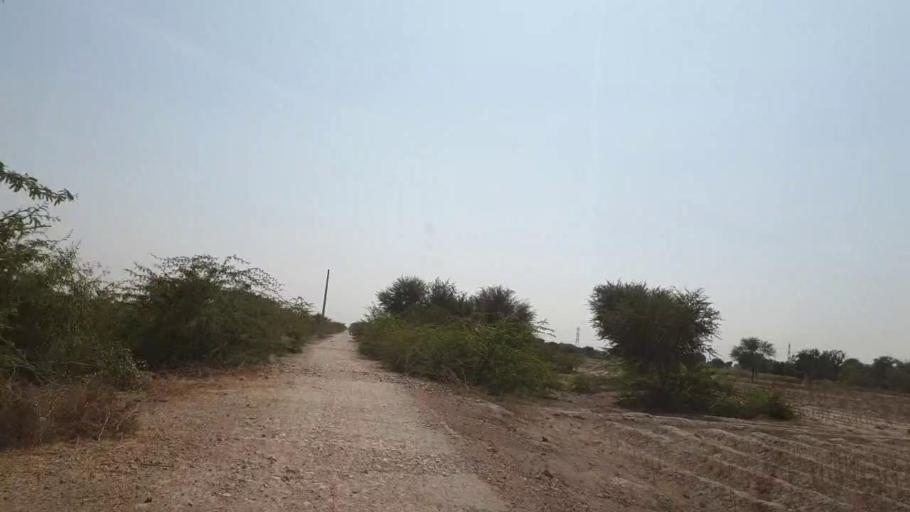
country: PK
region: Sindh
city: Nabisar
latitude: 25.0651
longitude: 69.5526
